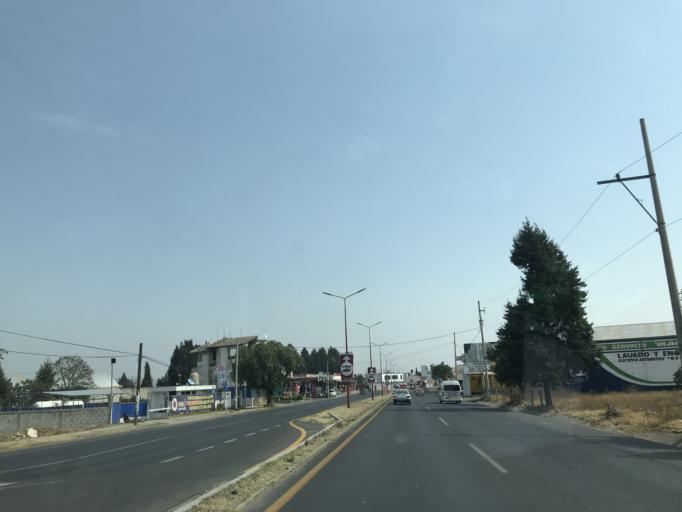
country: MX
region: Tlaxcala
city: La Magdalena Tlaltelulco
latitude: 19.2832
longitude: -98.1959
